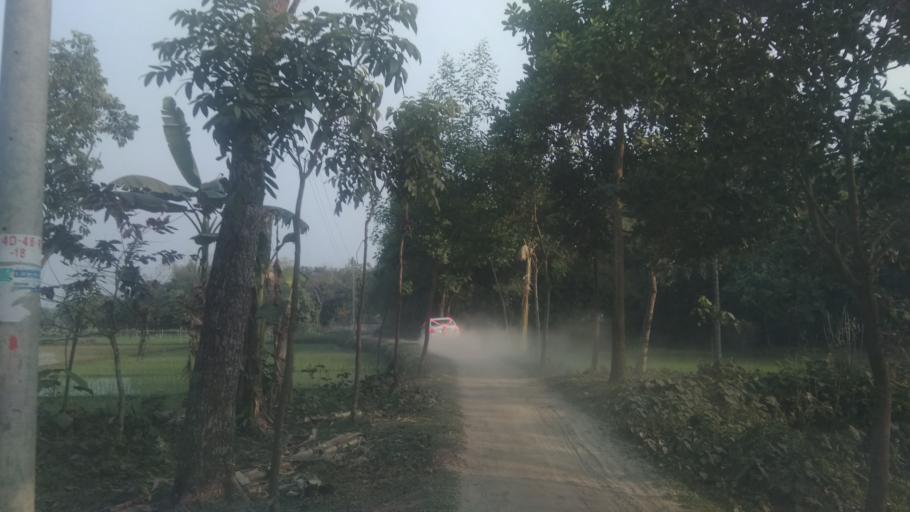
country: BD
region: Dhaka
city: Netrakona
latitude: 24.7733
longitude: 90.6113
